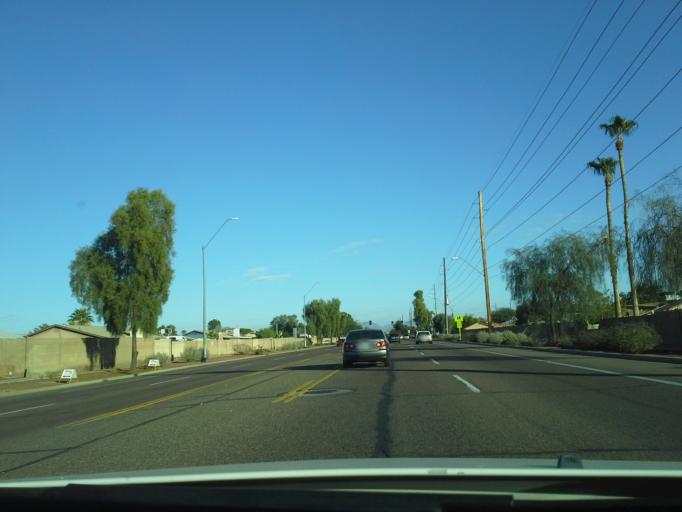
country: US
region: Arizona
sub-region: Maricopa County
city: Glendale
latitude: 33.6546
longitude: -112.0937
